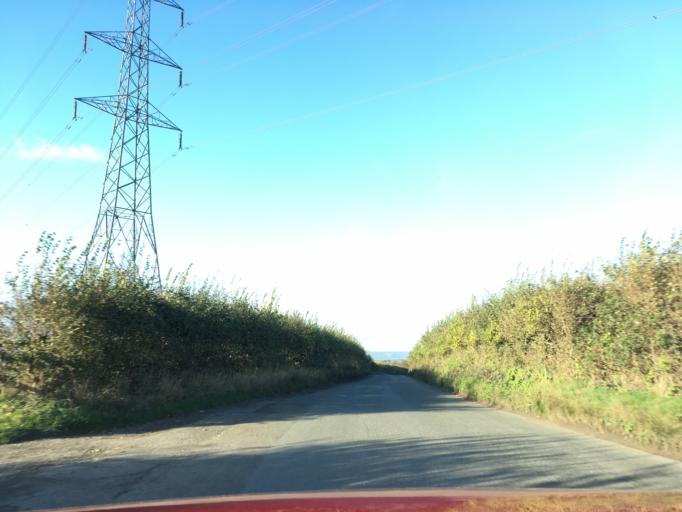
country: GB
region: England
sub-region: South Gloucestershire
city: Thornbury
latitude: 51.6232
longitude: -2.5097
